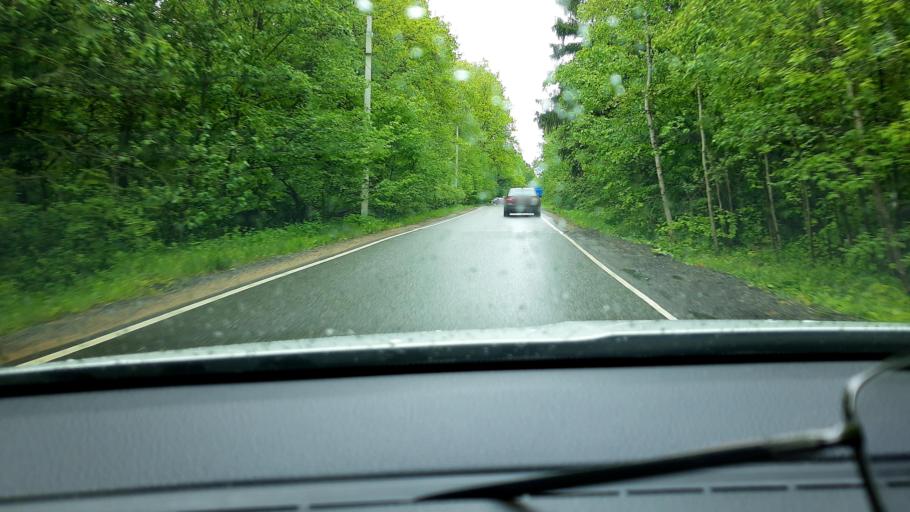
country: RU
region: Moskovskaya
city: Nikolina Gora
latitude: 55.7608
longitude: 36.9818
